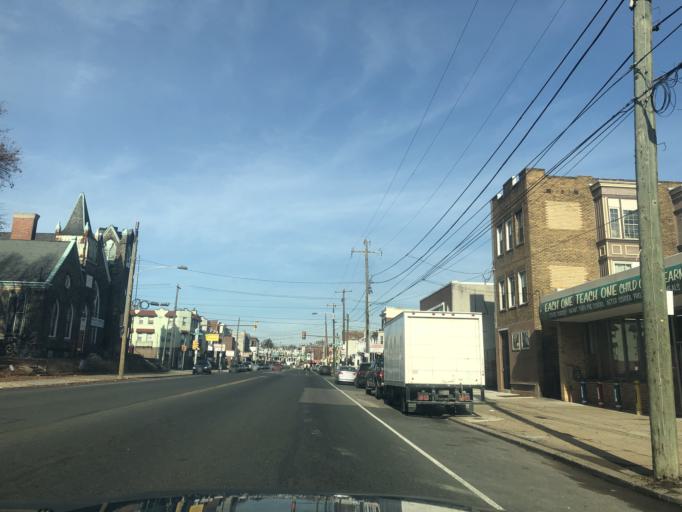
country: US
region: Pennsylvania
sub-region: Delaware County
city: Millbourne
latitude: 39.9696
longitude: -75.2453
